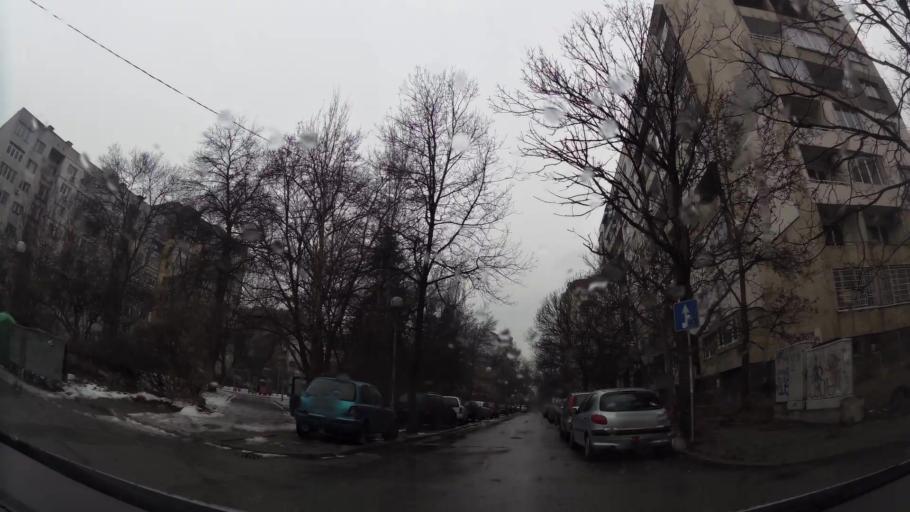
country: BG
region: Sofia-Capital
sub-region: Stolichna Obshtina
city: Sofia
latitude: 42.6708
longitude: 23.2985
